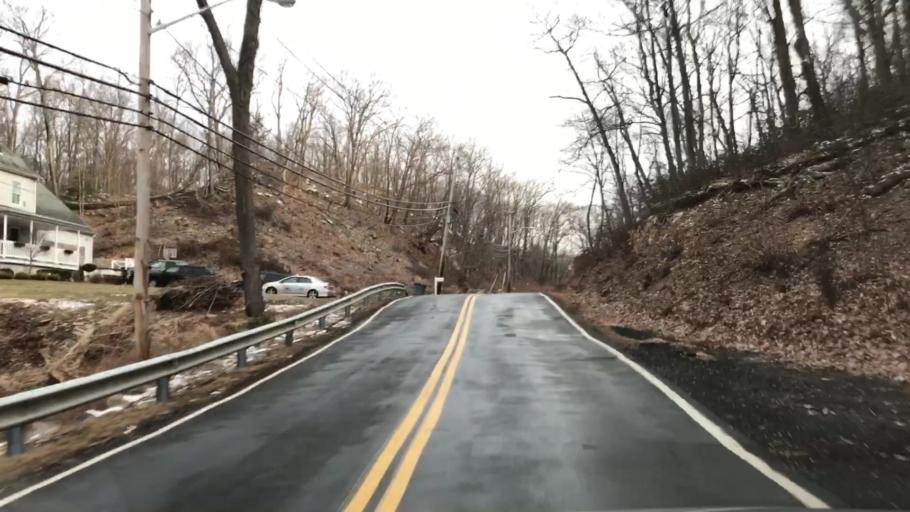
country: US
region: New York
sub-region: Rockland County
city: Thiells
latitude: 41.2235
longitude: -74.0469
